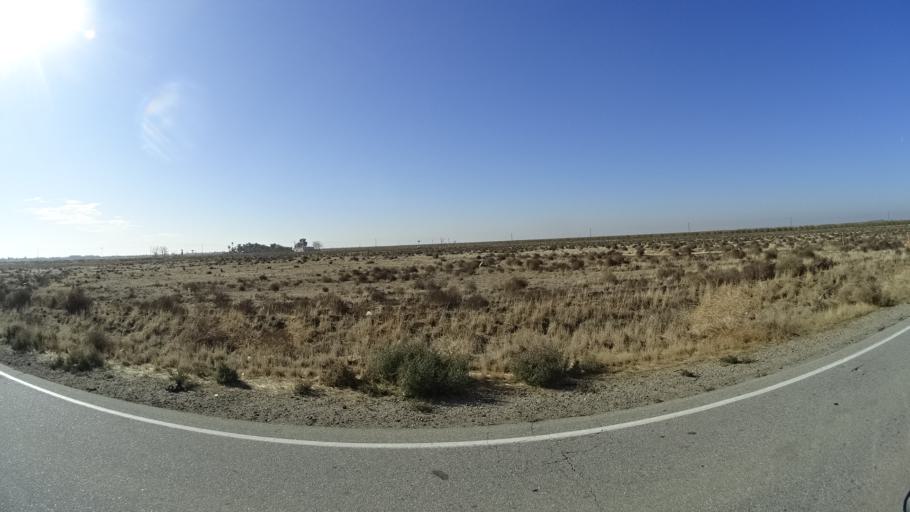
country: US
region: California
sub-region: Kern County
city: Rosedale
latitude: 35.4312
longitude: -119.1495
